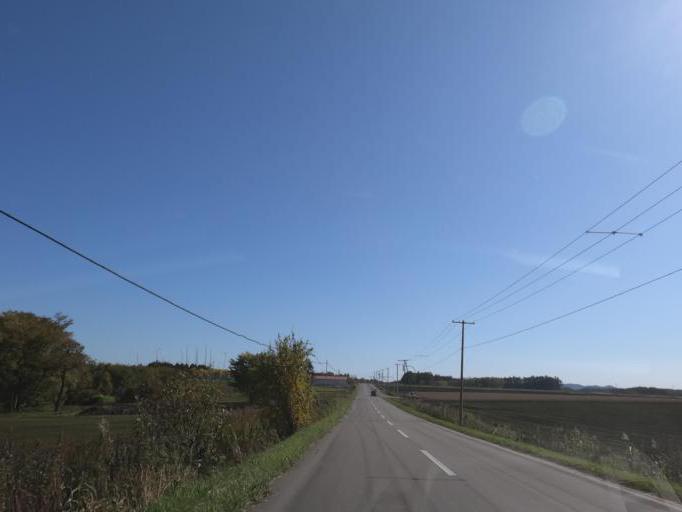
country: JP
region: Hokkaido
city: Obihiro
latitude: 42.8064
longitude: 143.2566
